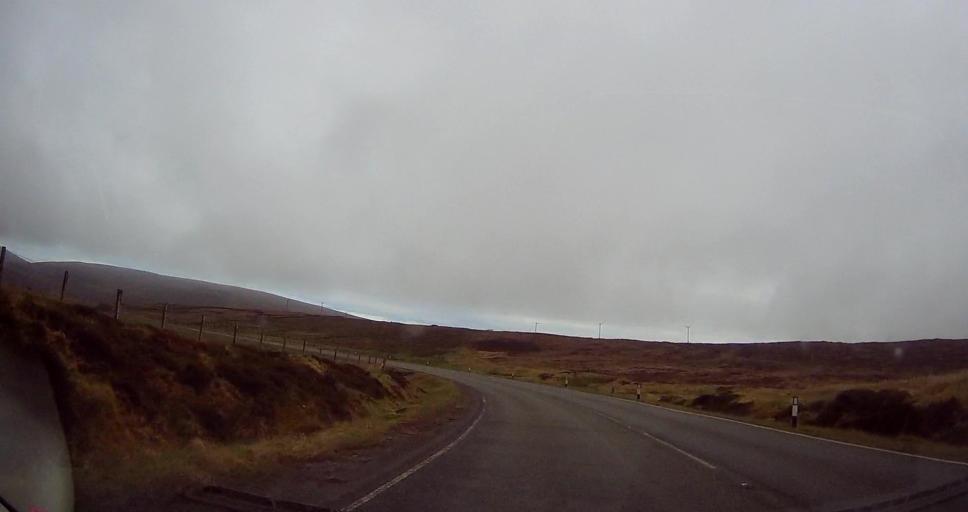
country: GB
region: Scotland
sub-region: Shetland Islands
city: Lerwick
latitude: 60.1396
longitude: -1.2214
